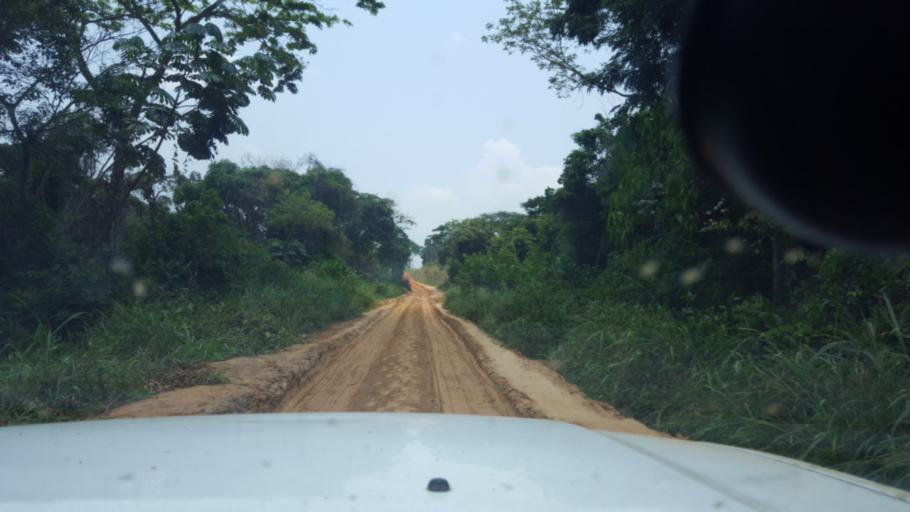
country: CD
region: Bandundu
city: Mushie
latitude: -3.7533
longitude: 16.6278
